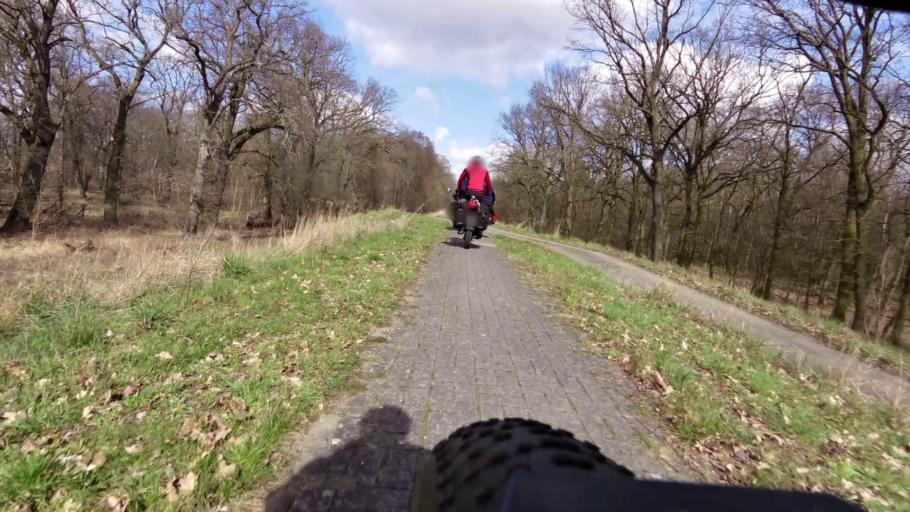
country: DE
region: Brandenburg
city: Lebus
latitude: 52.3923
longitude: 14.5398
